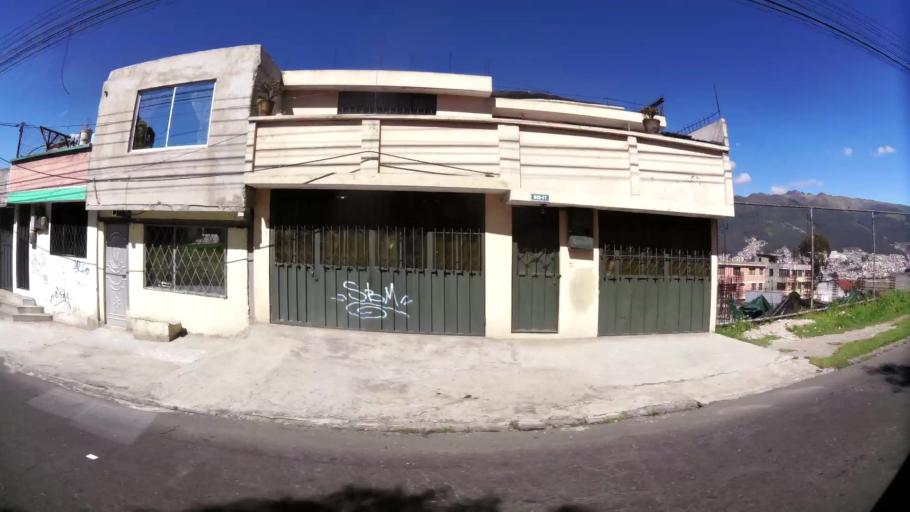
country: EC
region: Pichincha
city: Quito
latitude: -0.1506
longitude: -78.4662
